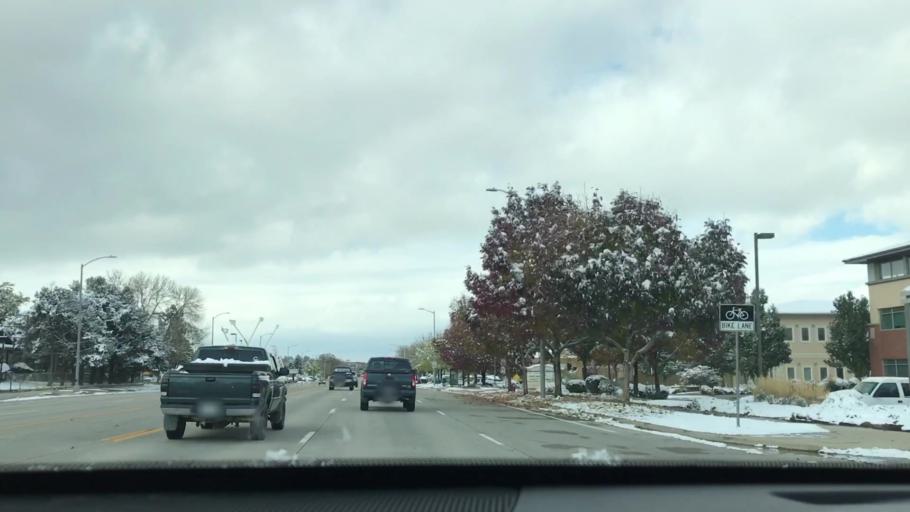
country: US
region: Colorado
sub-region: Boulder County
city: Longmont
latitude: 40.1480
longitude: -105.1024
